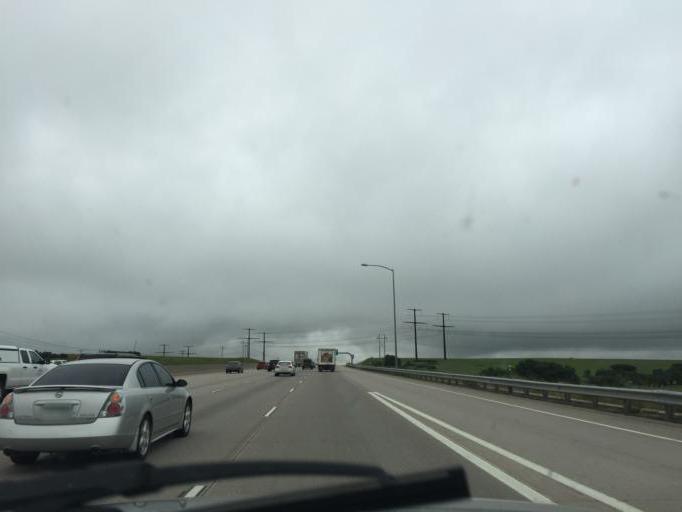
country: US
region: Colorado
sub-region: Douglas County
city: Castle Pines
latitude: 39.4544
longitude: -104.8752
